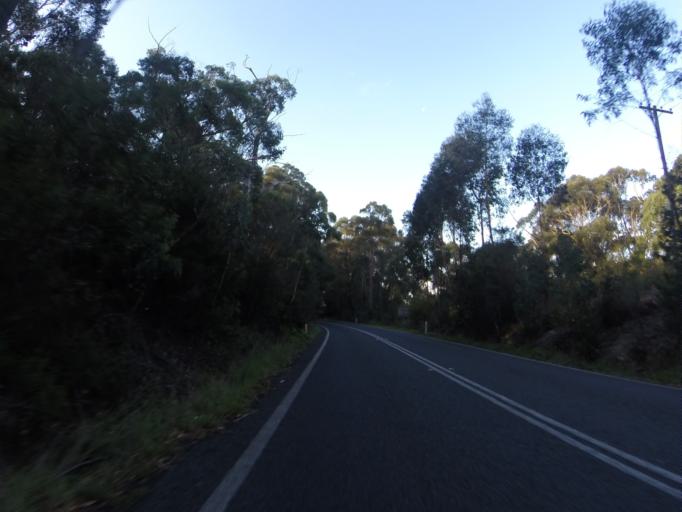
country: AU
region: New South Wales
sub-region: Shoalhaven Shire
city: Kangaroo Valley
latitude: -34.6578
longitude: 150.4895
